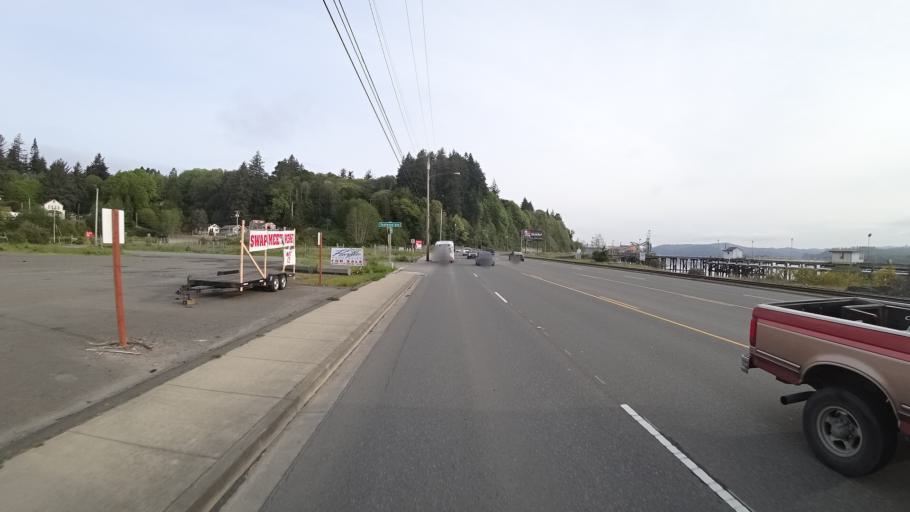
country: US
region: Oregon
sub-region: Coos County
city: Coos Bay
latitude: 43.3839
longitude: -124.2209
